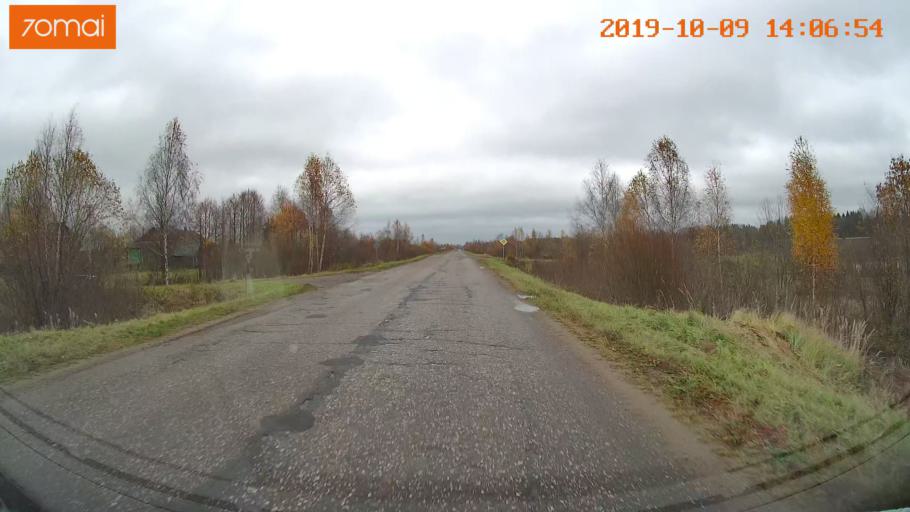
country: RU
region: Kostroma
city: Buy
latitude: 58.4672
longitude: 41.4159
